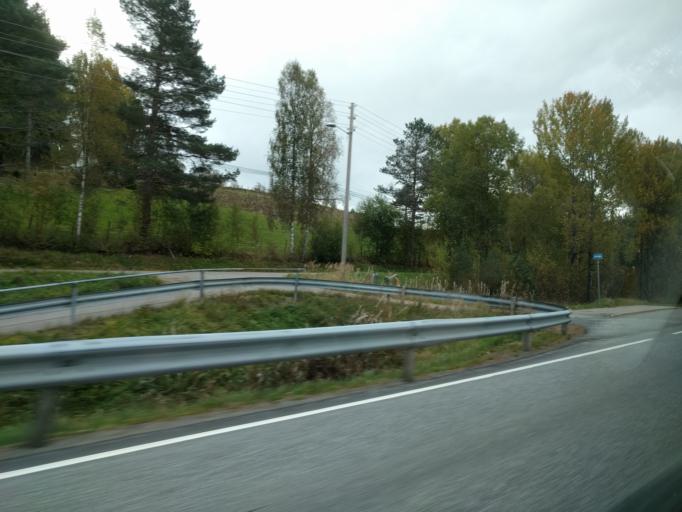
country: NO
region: Aust-Agder
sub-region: Iveland
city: Birketveit
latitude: 58.3876
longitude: 7.7387
